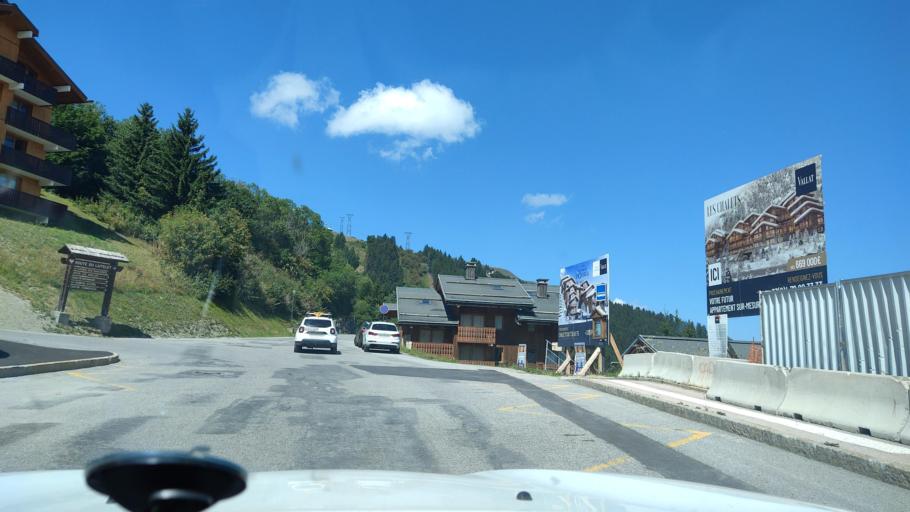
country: FR
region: Rhone-Alpes
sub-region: Departement de la Savoie
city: Meribel
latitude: 45.3747
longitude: 6.5746
